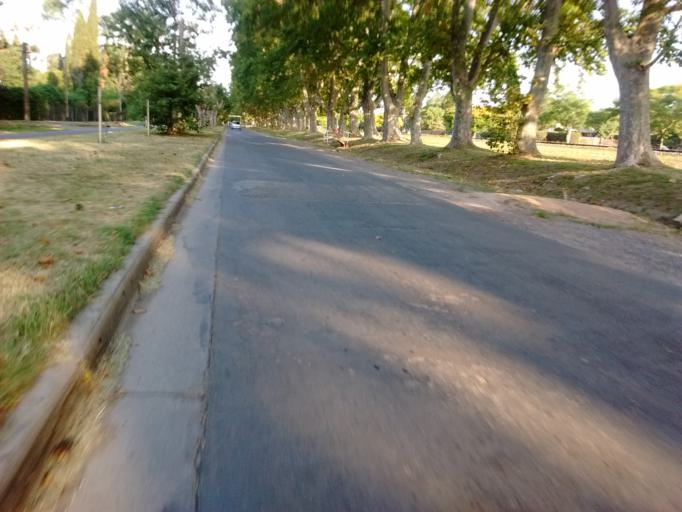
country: AR
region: Santa Fe
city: Funes
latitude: -32.9182
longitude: -60.8023
